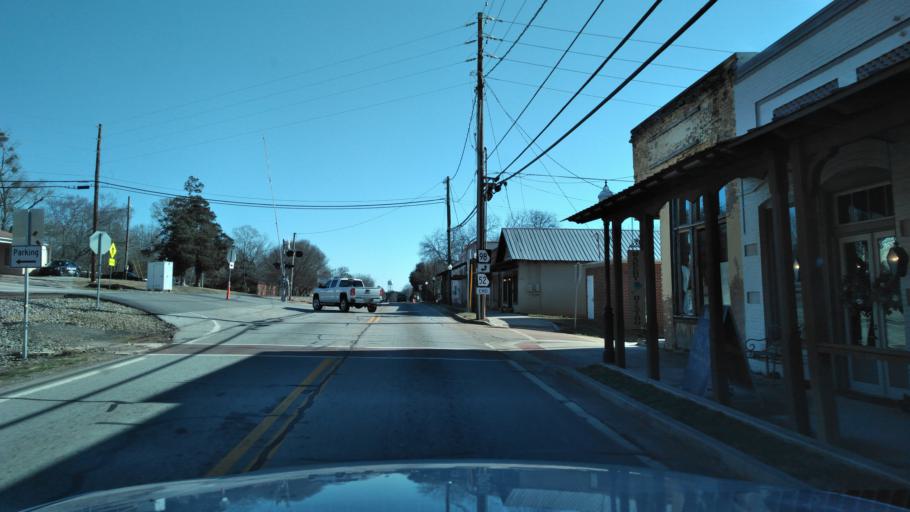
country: US
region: Georgia
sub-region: Banks County
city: Maysville
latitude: 34.2531
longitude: -83.5619
